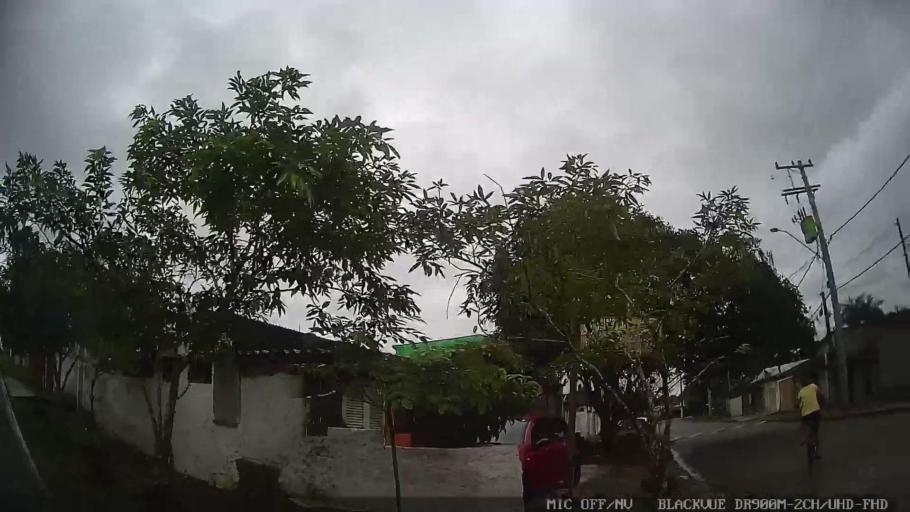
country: BR
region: Sao Paulo
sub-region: Itanhaem
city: Itanhaem
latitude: -24.1796
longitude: -46.8258
